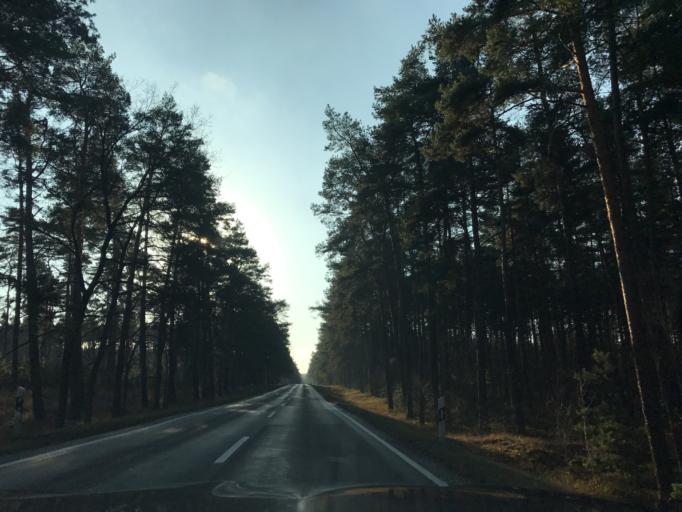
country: DE
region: Brandenburg
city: Wenzlow
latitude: 52.3175
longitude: 12.4809
